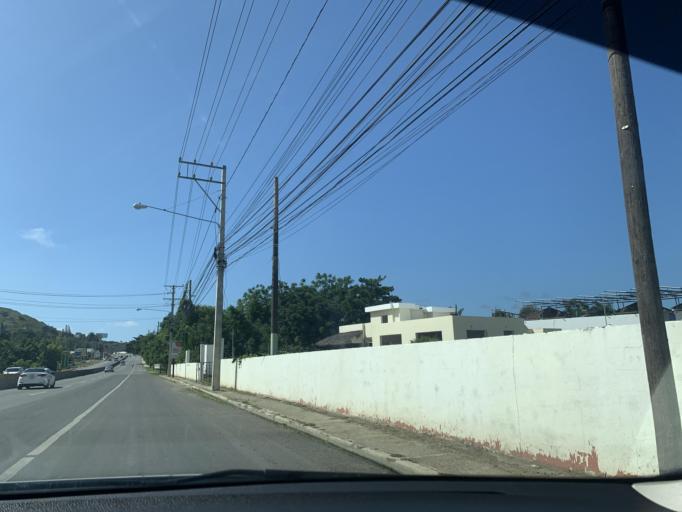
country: DO
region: Puerto Plata
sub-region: Puerto Plata
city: Puerto Plata
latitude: 19.8082
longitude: -70.7295
